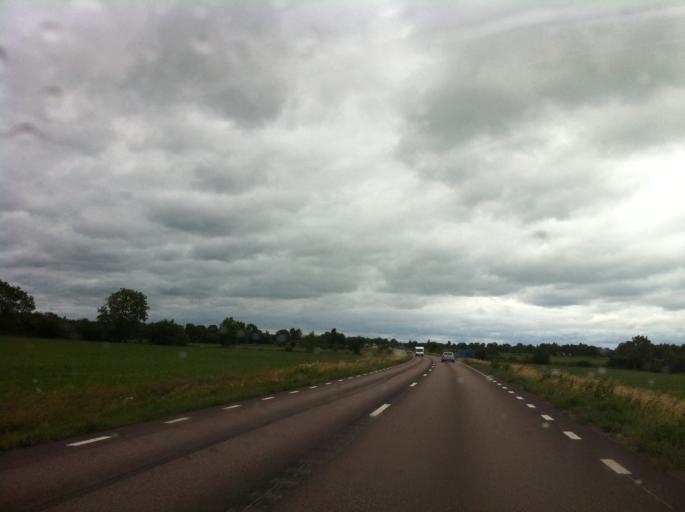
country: SE
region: Kalmar
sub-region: Borgholms Kommun
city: Borgholm
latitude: 57.1229
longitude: 16.9669
